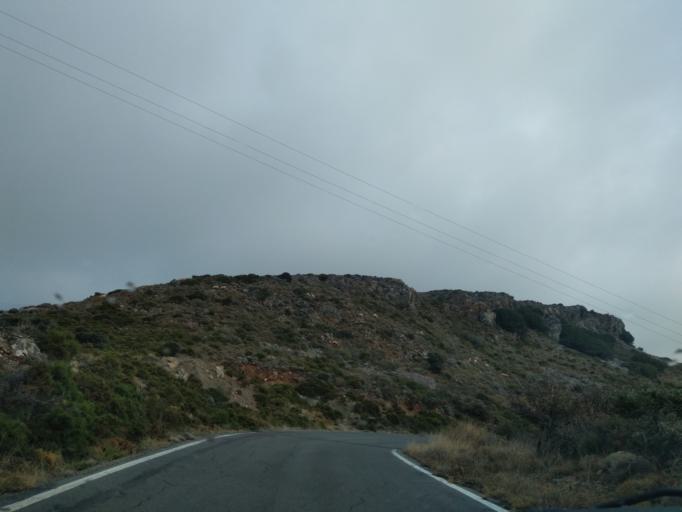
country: GR
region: Crete
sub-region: Nomos Lasithiou
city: Siteia
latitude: 35.1529
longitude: 26.0181
